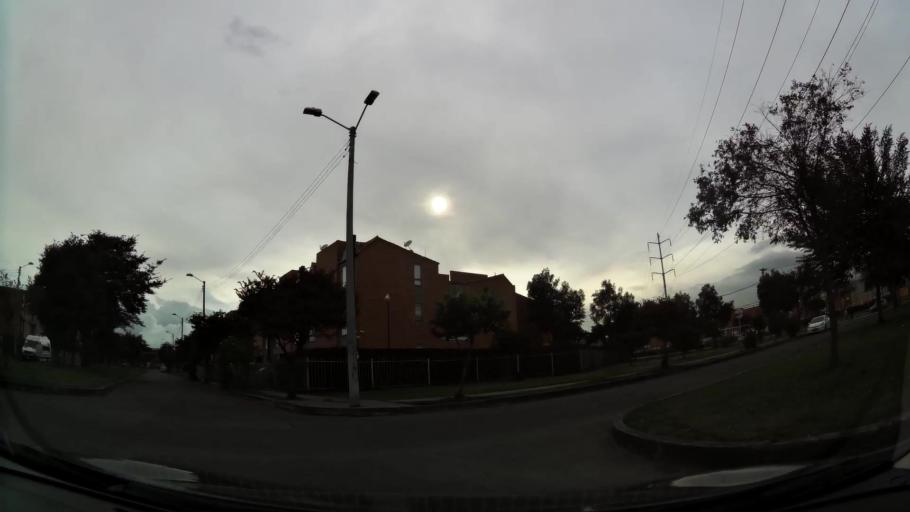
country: CO
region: Cundinamarca
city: Mosquera
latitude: 4.7089
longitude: -74.2256
